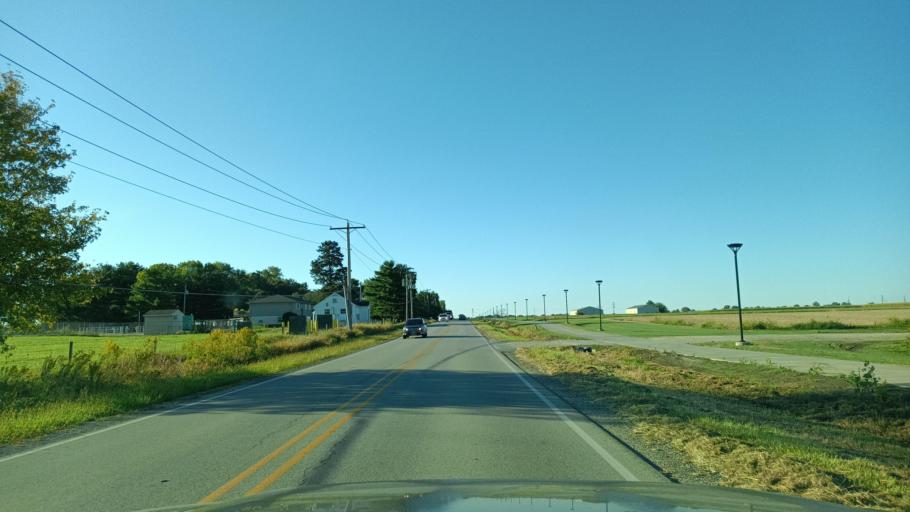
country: US
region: Illinois
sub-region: Champaign County
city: Savoy
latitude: 40.0811
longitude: -88.2385
